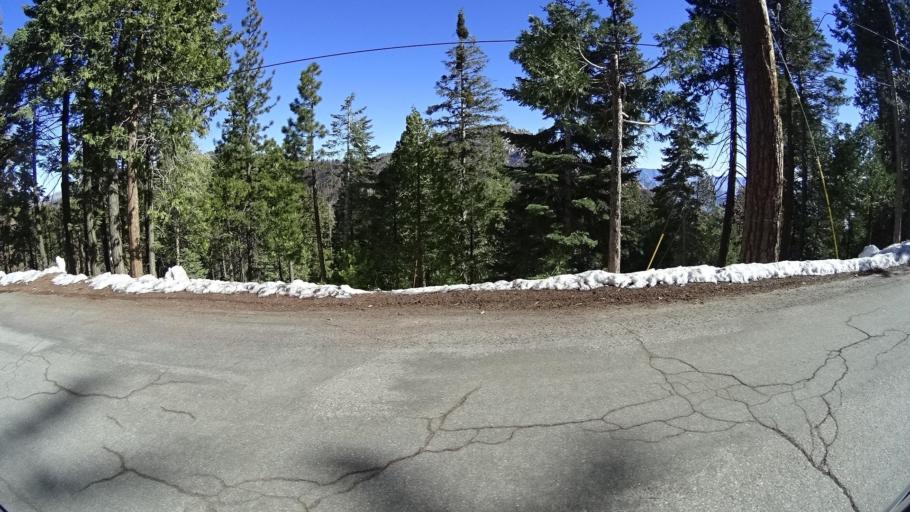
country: US
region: California
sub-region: Kern County
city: Alta Sierra
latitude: 35.7302
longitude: -118.5582
